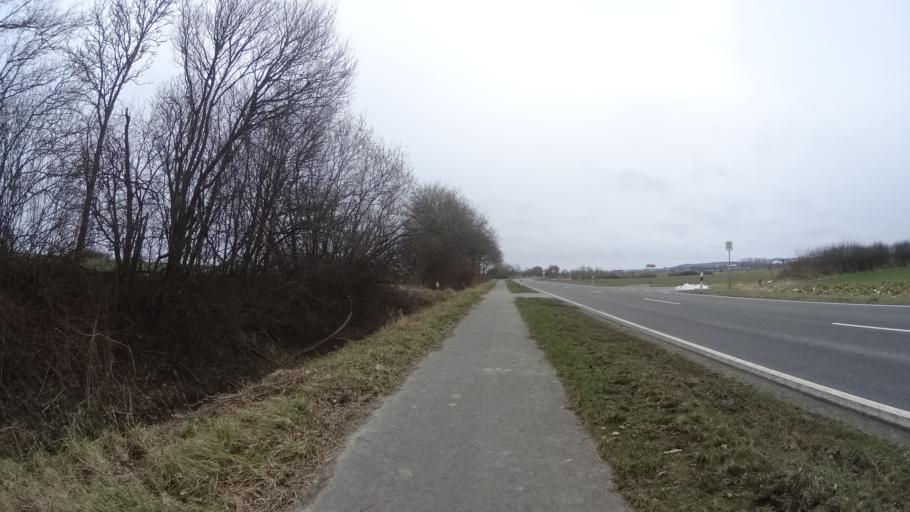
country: DE
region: Schleswig-Holstein
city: Hohenfelde
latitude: 54.3615
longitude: 10.5214
